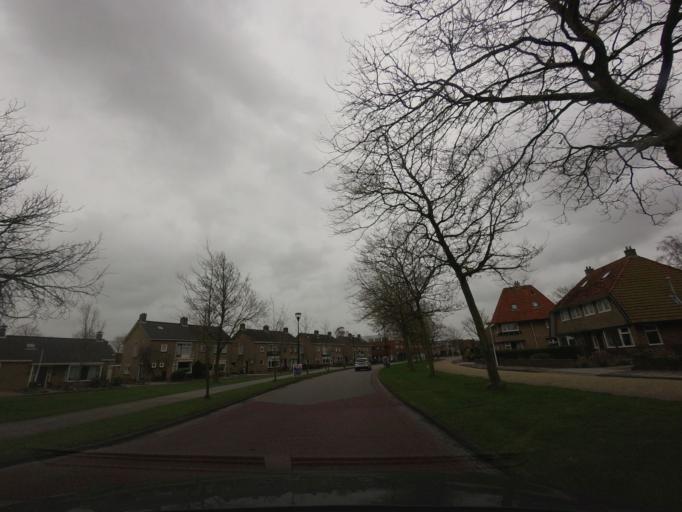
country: NL
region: Friesland
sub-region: Gemeente Franekeradeel
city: Franeker
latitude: 53.1919
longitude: 5.5416
